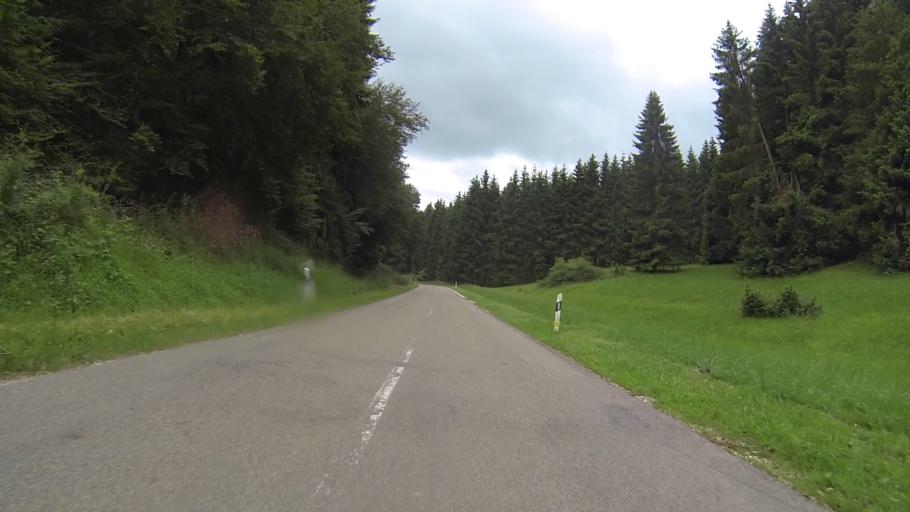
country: DE
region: Baden-Wuerttemberg
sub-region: Regierungsbezirk Stuttgart
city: Gerstetten
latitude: 48.6806
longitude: 9.9950
